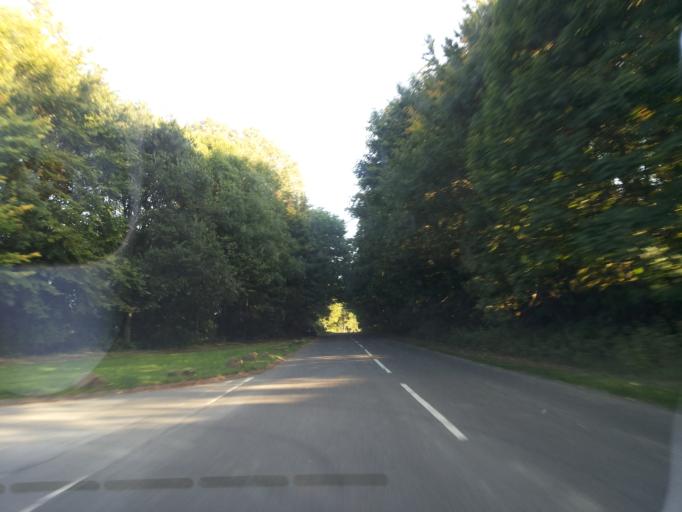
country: GB
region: England
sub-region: Derbyshire
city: Tibshelf
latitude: 53.1699
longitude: -1.3249
